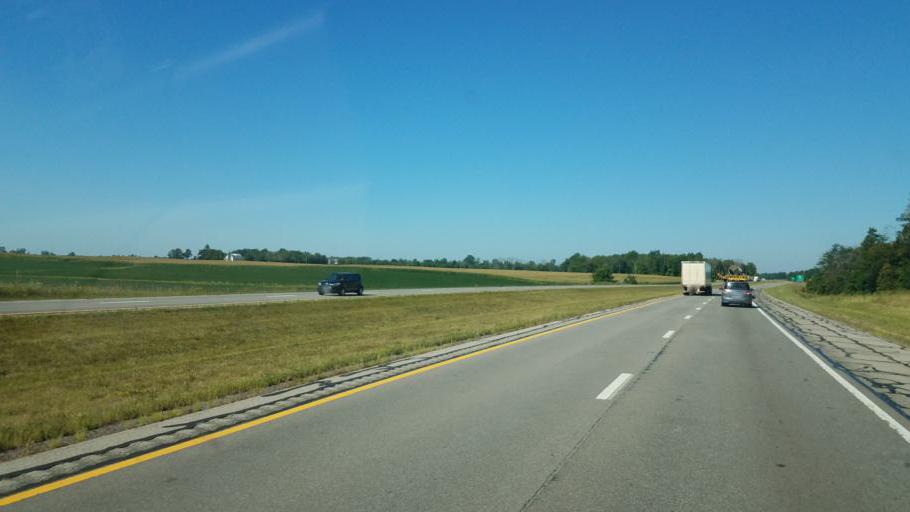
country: US
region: Ohio
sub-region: Crawford County
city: Crestline
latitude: 40.7619
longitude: -82.7135
